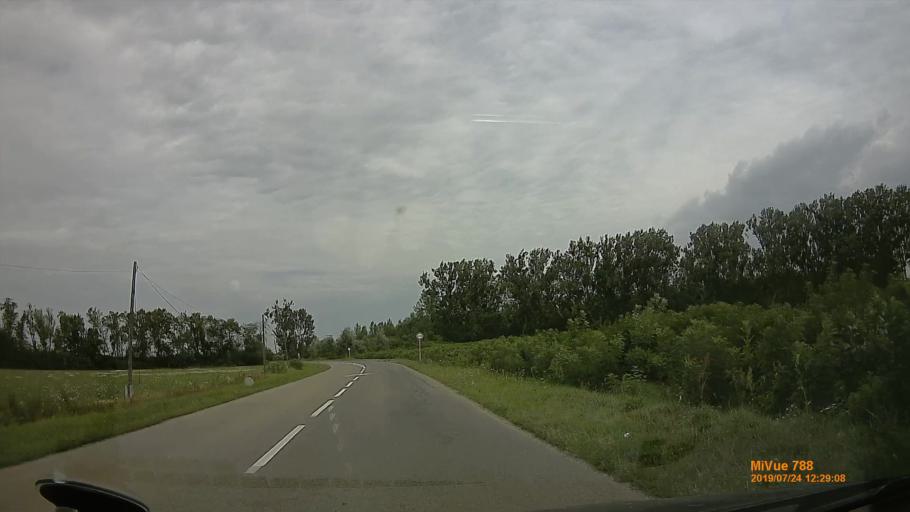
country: HU
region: Szabolcs-Szatmar-Bereg
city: Vasarosnameny
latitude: 48.1480
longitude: 22.3474
